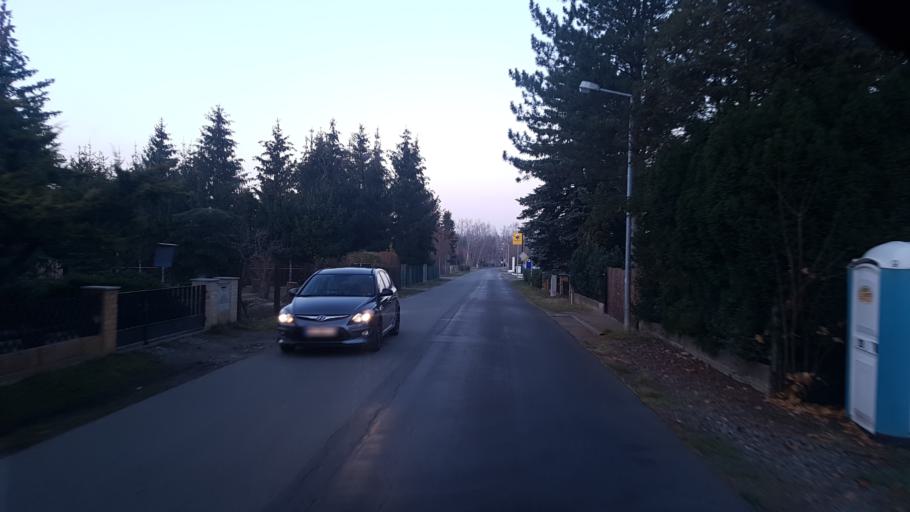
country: DE
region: Brandenburg
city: Lauchhammer
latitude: 51.5025
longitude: 13.7558
